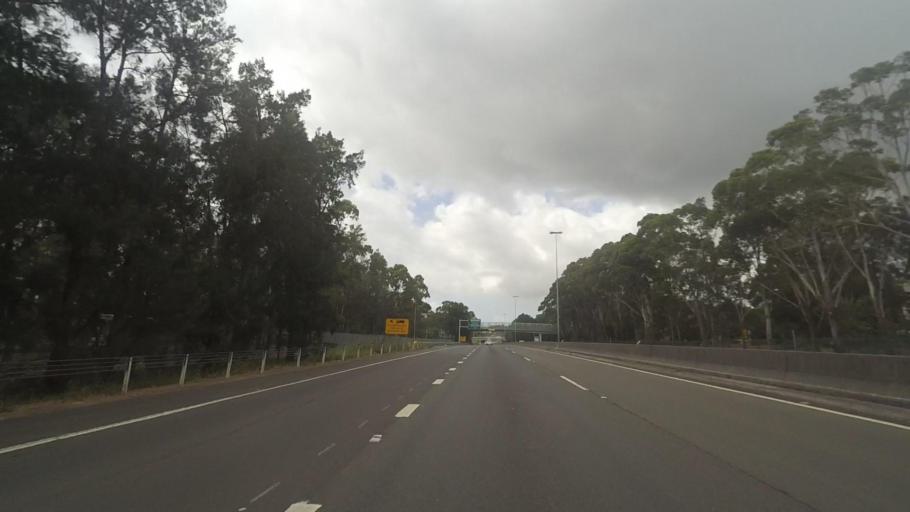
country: AU
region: New South Wales
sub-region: Wollongong
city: Gwynneville
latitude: -34.4069
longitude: 150.8837
